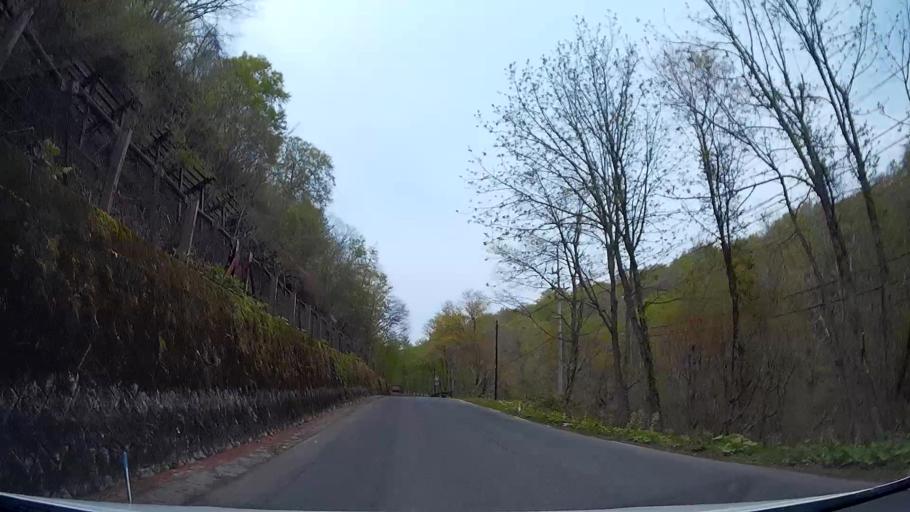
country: JP
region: Akita
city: Hanawa
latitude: 40.3917
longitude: 140.8779
